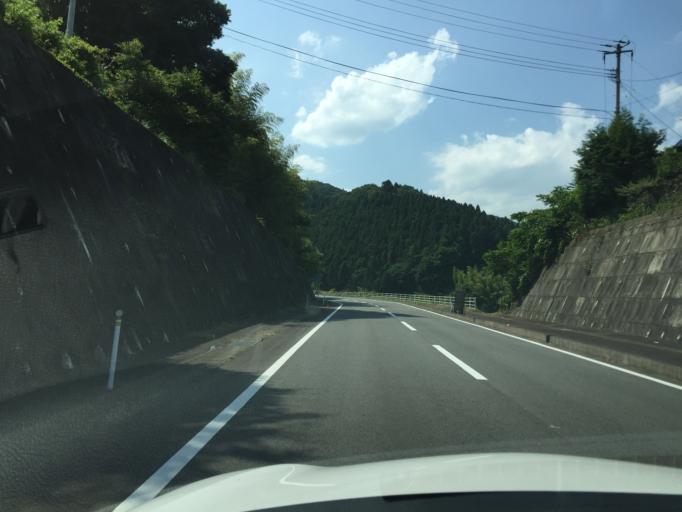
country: JP
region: Ibaraki
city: Kitaibaraki
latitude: 36.9380
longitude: 140.7309
